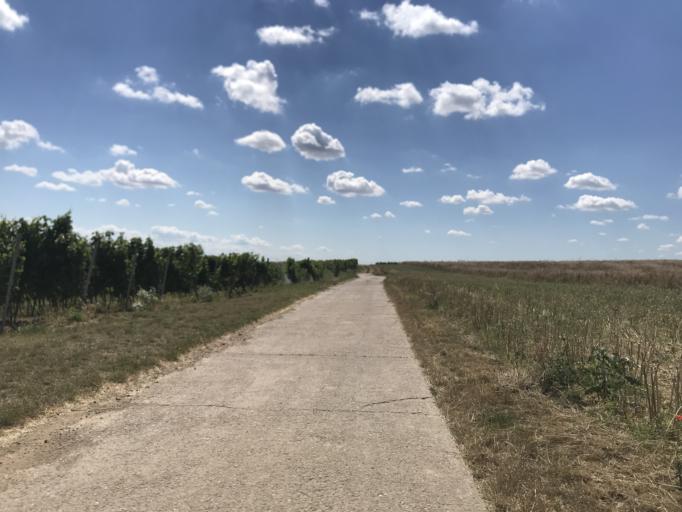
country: DE
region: Rheinland-Pfalz
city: Bubenheim
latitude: 49.9176
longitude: 8.0679
